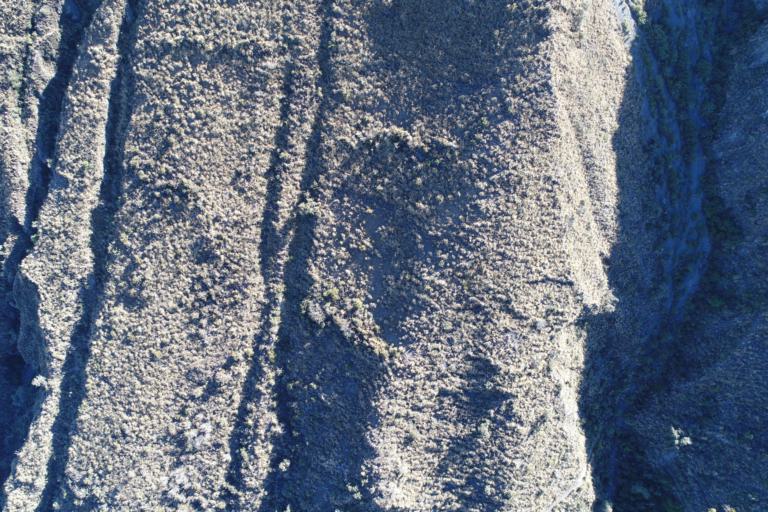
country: BO
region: La Paz
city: Viloco
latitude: -16.8199
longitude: -67.5494
